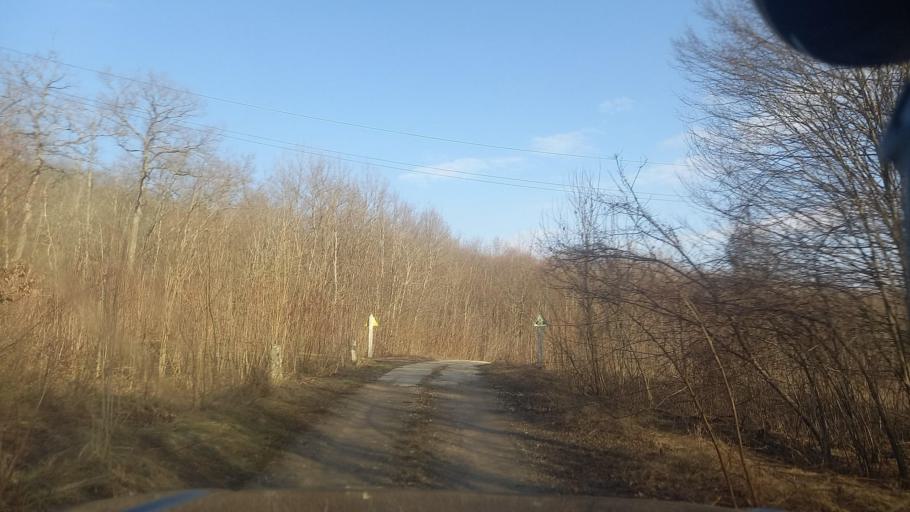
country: RU
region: Krasnodarskiy
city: Smolenskaya
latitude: 44.7052
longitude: 38.7850
